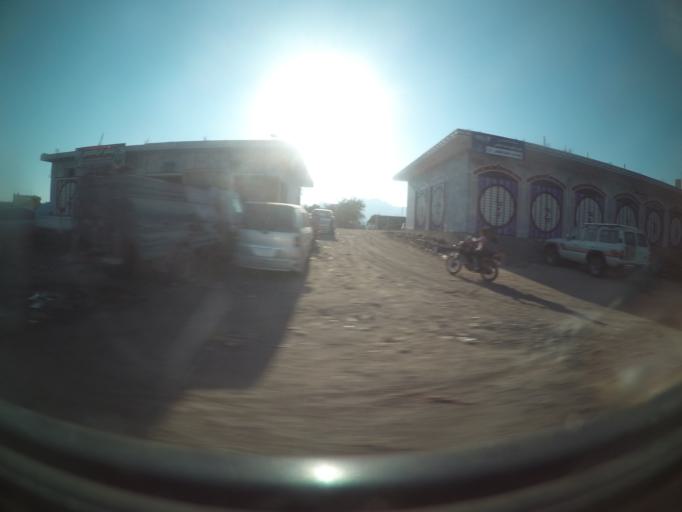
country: YE
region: Lahij
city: Habil ar Raydah
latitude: 13.6389
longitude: 44.8593
